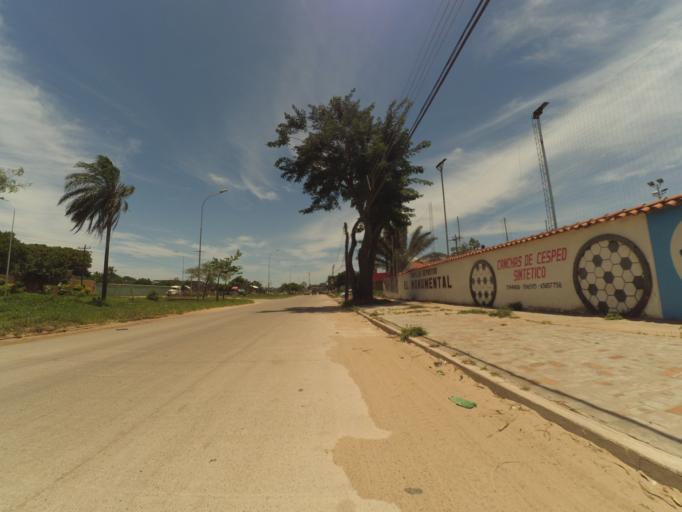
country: BO
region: Santa Cruz
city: Santa Cruz de la Sierra
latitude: -17.8100
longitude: -63.2216
